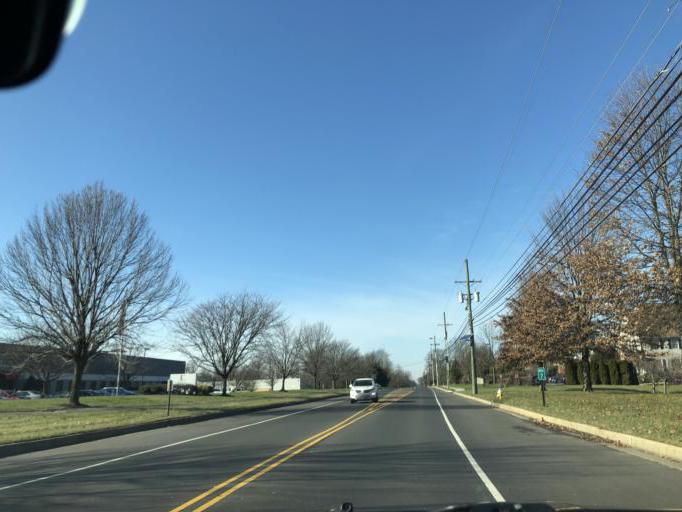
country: US
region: New Jersey
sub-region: Burlington County
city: Moorestown-Lenola
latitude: 39.9726
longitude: -74.9741
